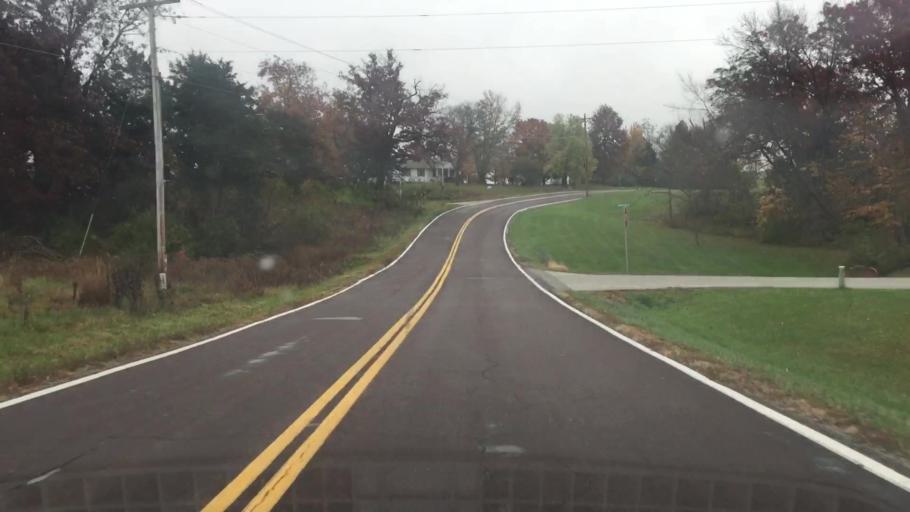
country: US
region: Missouri
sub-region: Callaway County
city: Fulton
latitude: 38.8190
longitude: -91.9073
